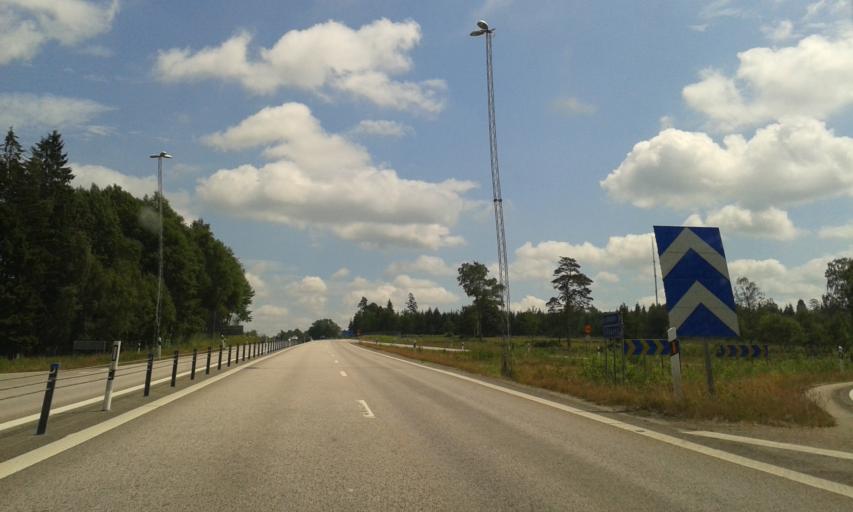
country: SE
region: Kronoberg
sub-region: Alvesta Kommun
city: Alvesta
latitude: 56.9218
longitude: 14.5679
